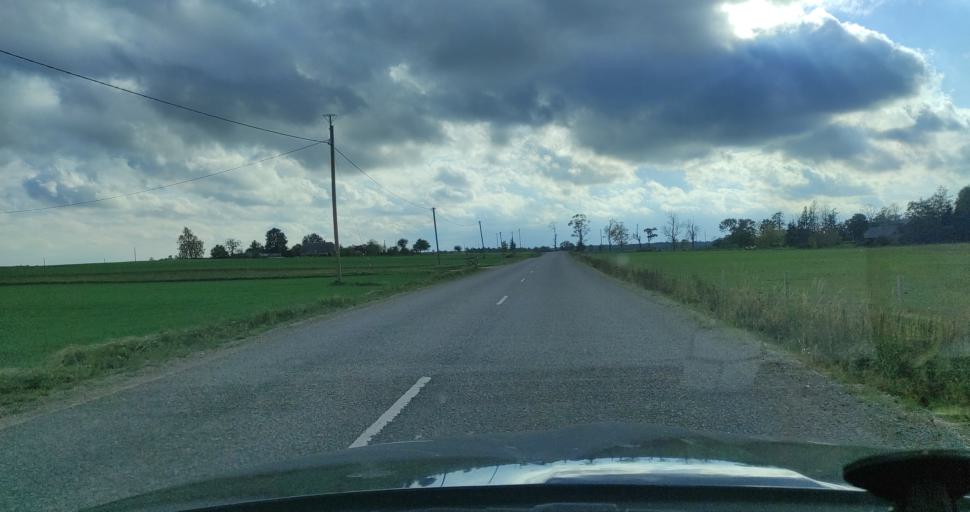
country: LV
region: Talsu Rajons
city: Sabile
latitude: 56.9441
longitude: 22.3979
